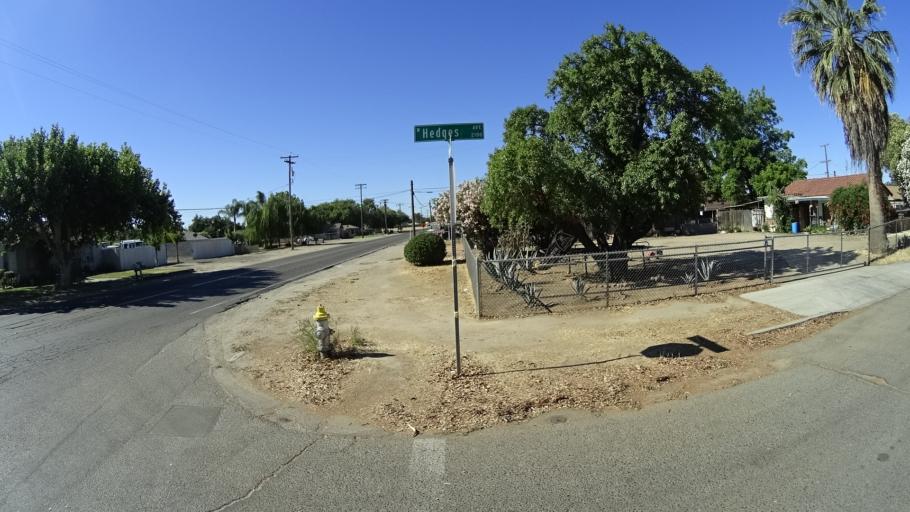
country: US
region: California
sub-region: Fresno County
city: West Park
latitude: 36.7593
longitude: -119.8357
